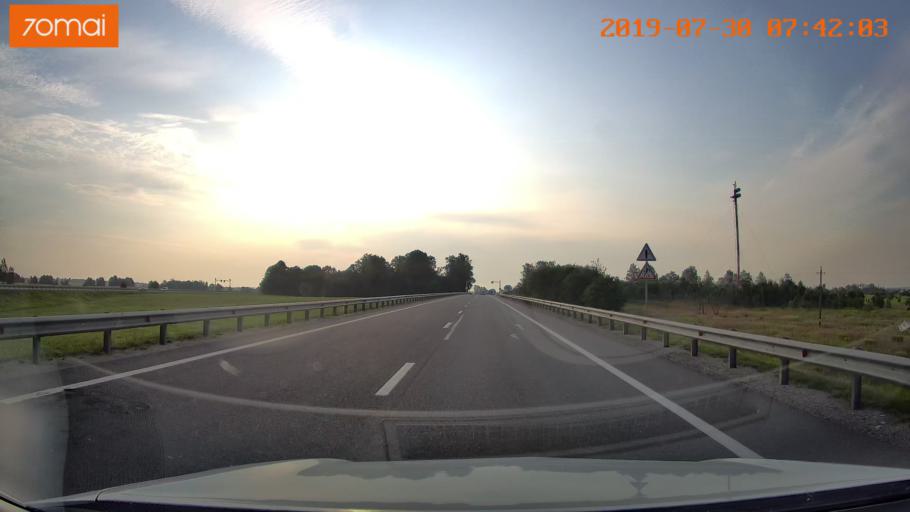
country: RU
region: Kaliningrad
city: Gvardeysk
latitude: 54.6478
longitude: 21.2683
